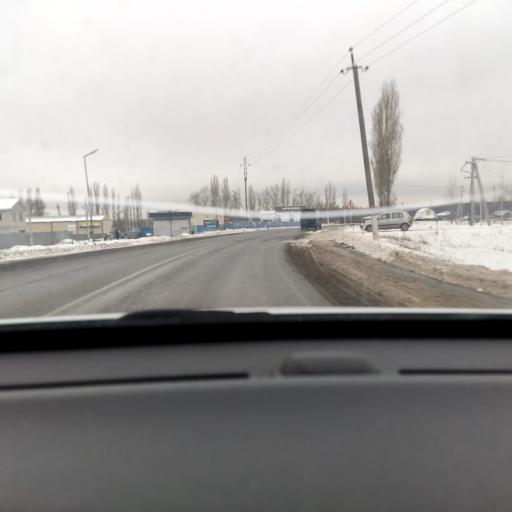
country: RU
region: Voronezj
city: Novaya Usman'
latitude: 51.6593
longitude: 39.4019
